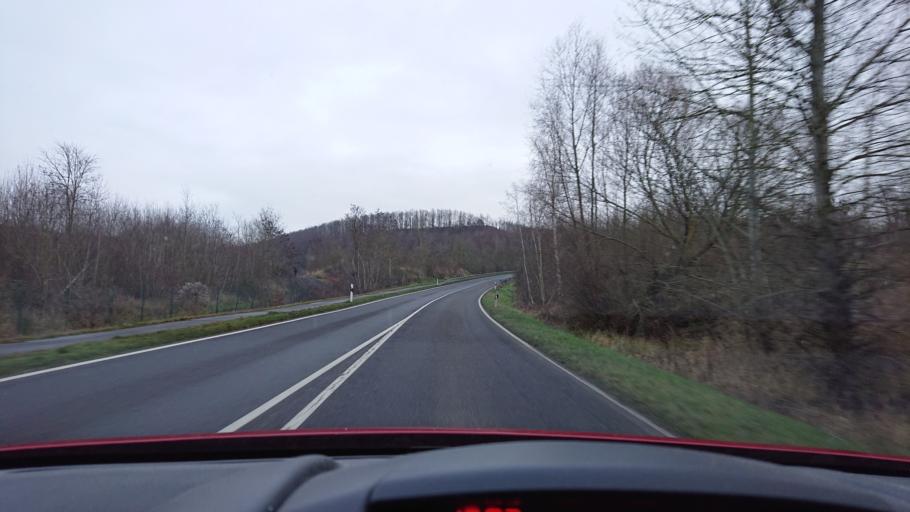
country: DE
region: North Rhine-Westphalia
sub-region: Regierungsbezirk Koln
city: Bergheim
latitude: 50.9608
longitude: 6.6877
